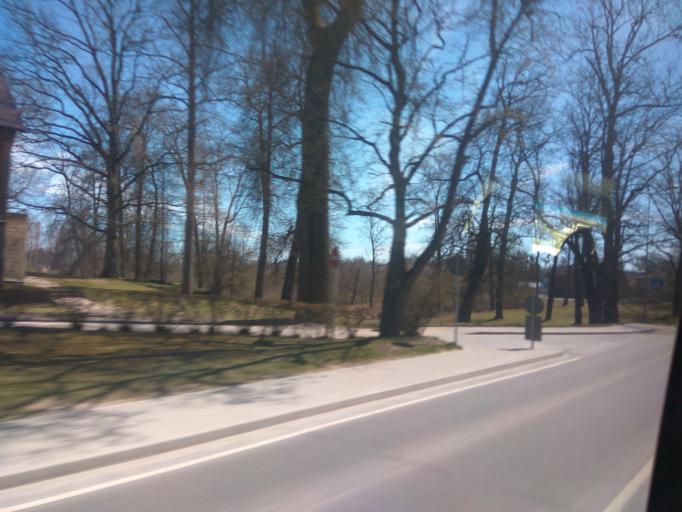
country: LV
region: Aluksnes Rajons
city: Aluksne
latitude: 57.4270
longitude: 27.0404
